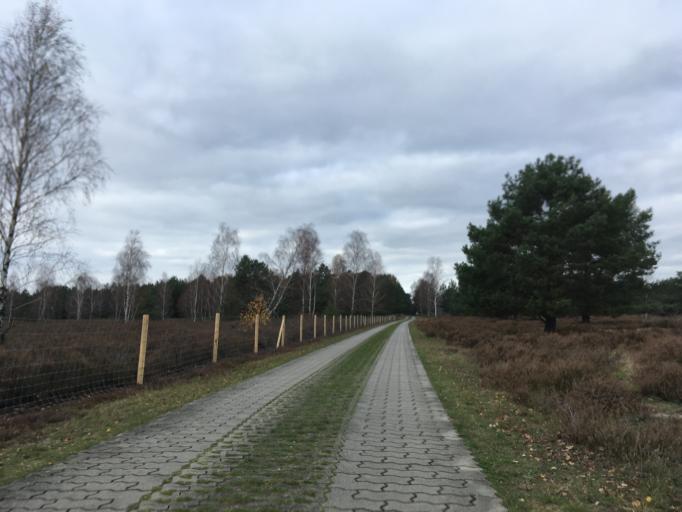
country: DE
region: Brandenburg
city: Tauer
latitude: 52.0129
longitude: 14.4903
